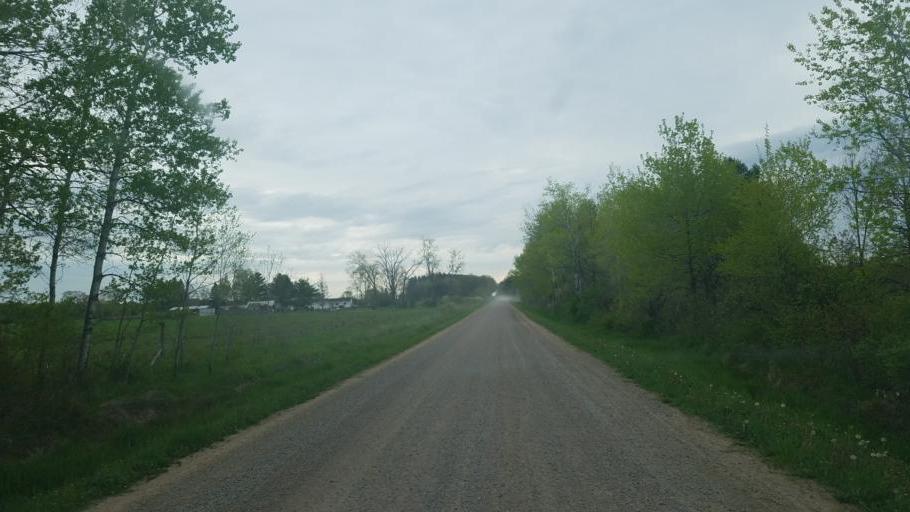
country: US
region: Wisconsin
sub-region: Clark County
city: Loyal
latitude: 44.6255
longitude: -90.4263
